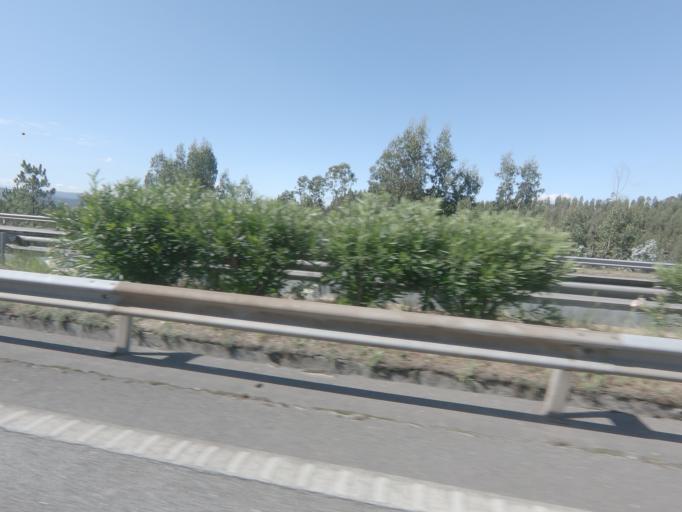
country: PT
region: Porto
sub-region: Paredes
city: Recarei
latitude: 41.1743
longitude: -8.4153
